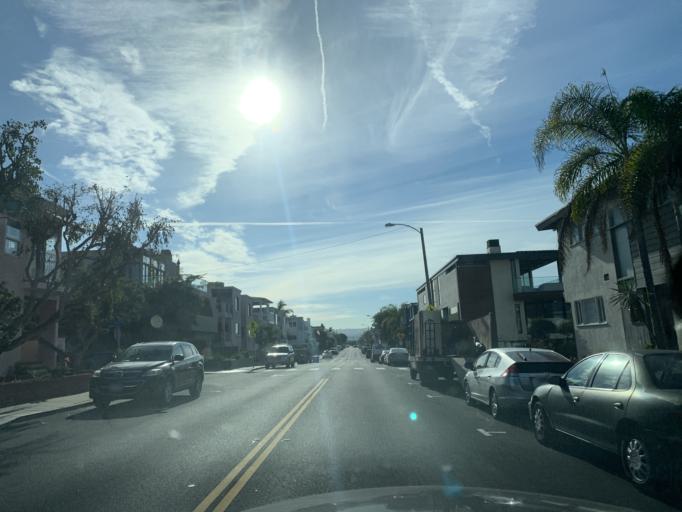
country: US
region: California
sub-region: Los Angeles County
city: Manhattan Beach
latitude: 33.8816
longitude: -118.4078
